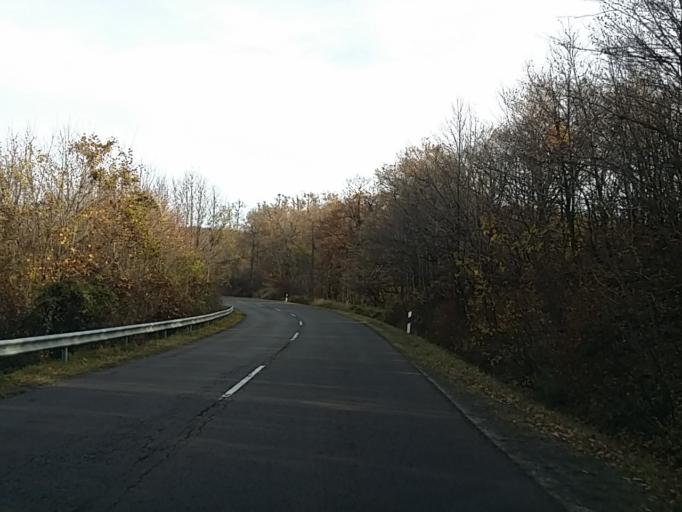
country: HU
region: Heves
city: Paradsasvar
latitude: 47.8611
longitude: 19.9704
